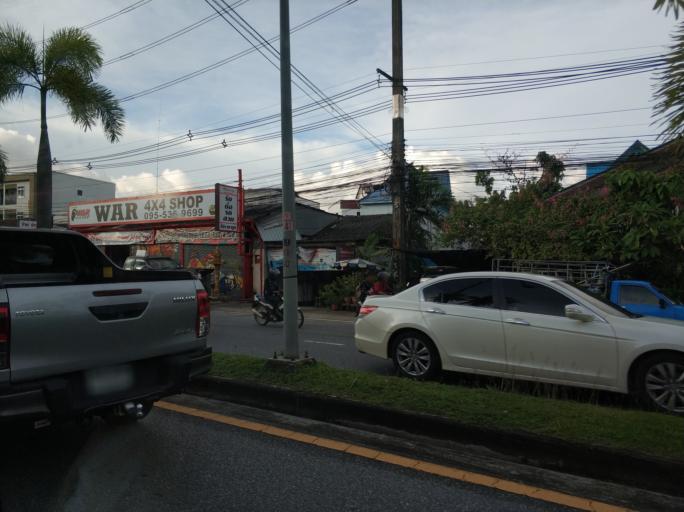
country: TH
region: Phuket
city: Kathu
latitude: 7.8996
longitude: 98.3548
